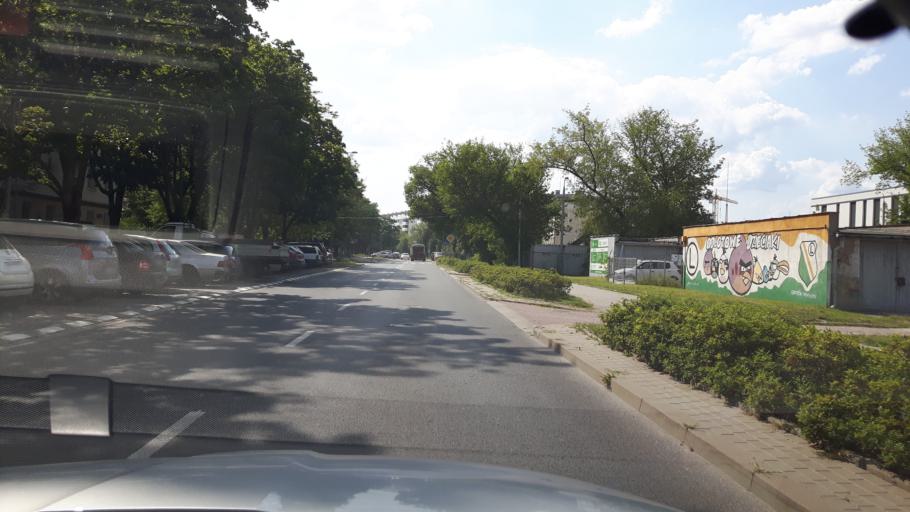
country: PL
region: Masovian Voivodeship
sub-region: Warszawa
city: Praga Poludnie
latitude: 52.2526
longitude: 21.0810
